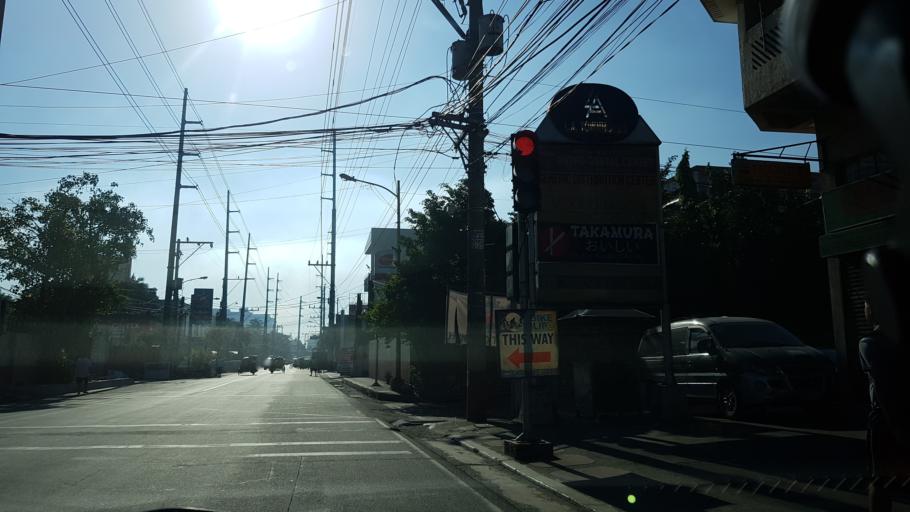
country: PH
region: Calabarzon
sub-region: Province of Rizal
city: Pateros
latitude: 14.5536
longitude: 121.0699
